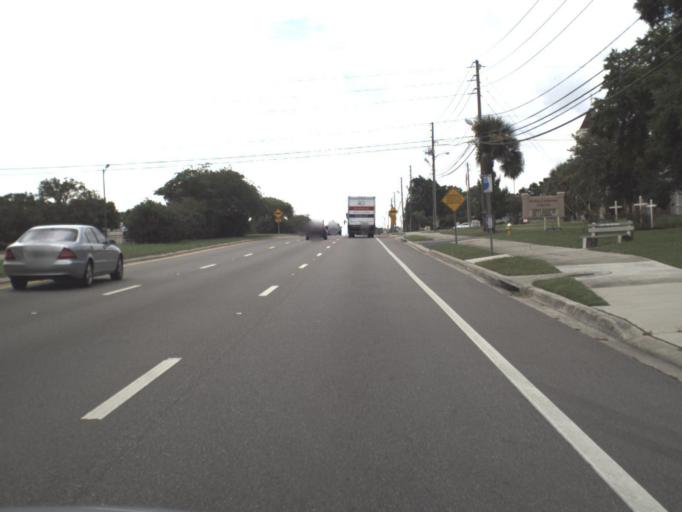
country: US
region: Florida
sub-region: Pinellas County
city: Saint George
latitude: 28.0368
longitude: -82.7092
